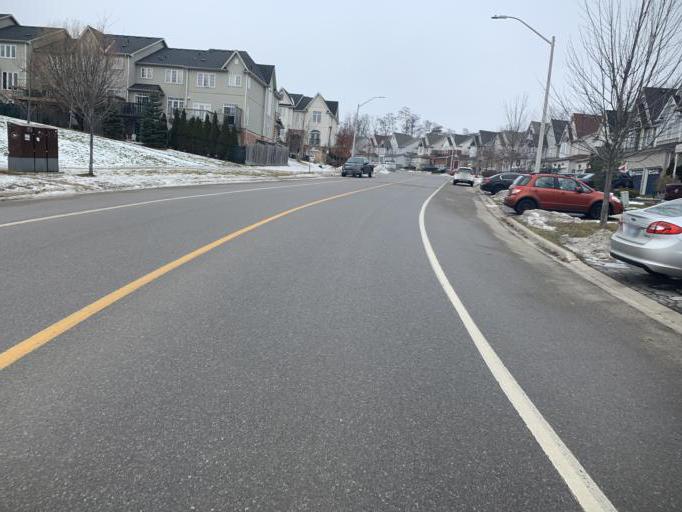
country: CA
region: Ontario
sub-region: Halton
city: Milton
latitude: 43.6603
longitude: -79.9208
